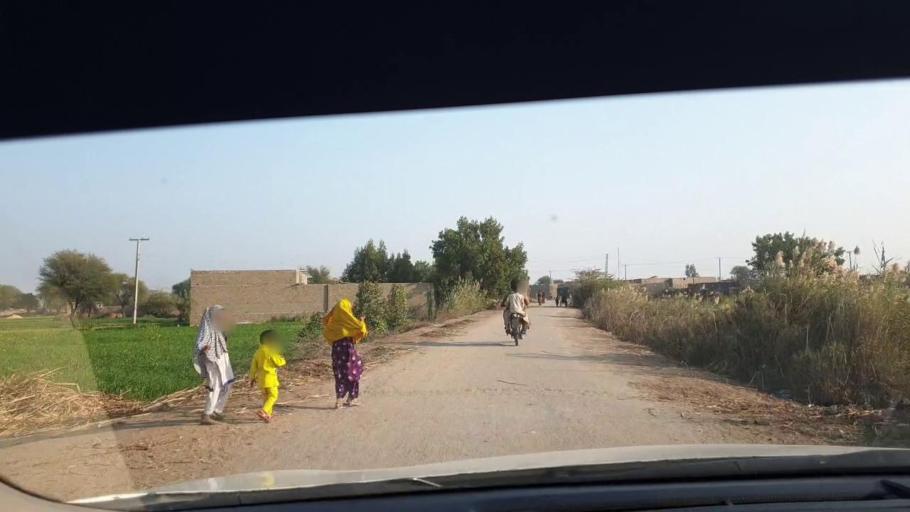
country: PK
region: Sindh
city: Berani
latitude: 25.8425
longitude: 68.7773
